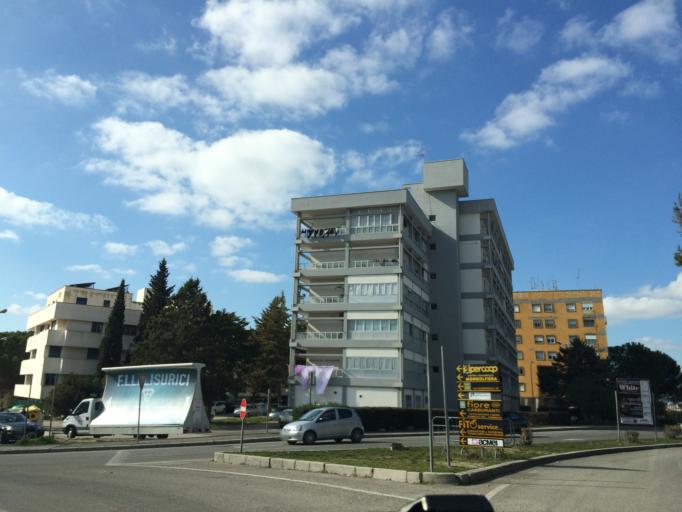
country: IT
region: Basilicate
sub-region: Provincia di Matera
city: Matera
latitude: 40.6738
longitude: 16.5865
